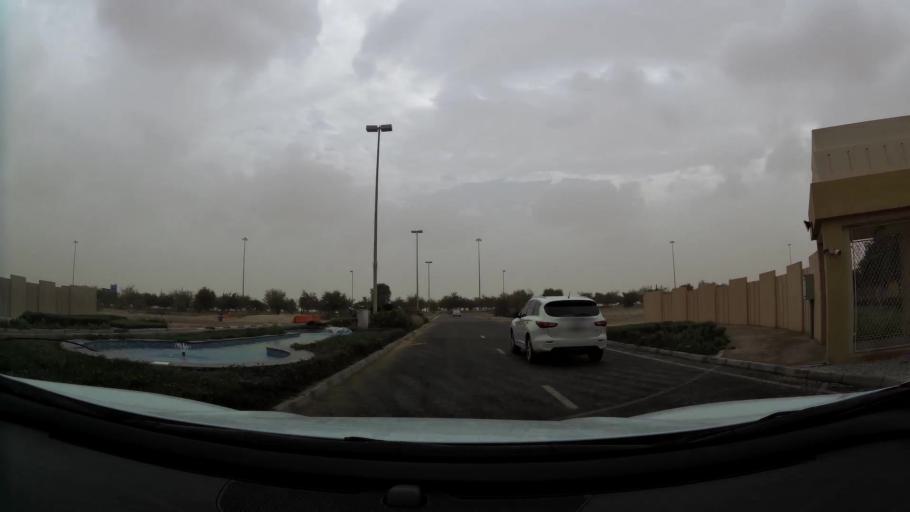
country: AE
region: Abu Dhabi
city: Abu Dhabi
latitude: 24.4537
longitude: 54.6769
